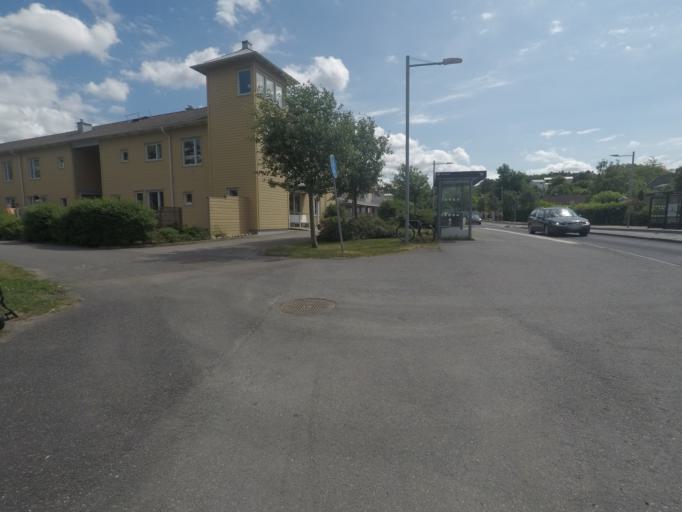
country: SE
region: Vaestra Goetaland
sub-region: Goteborg
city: Billdal
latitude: 57.5752
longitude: 11.9422
